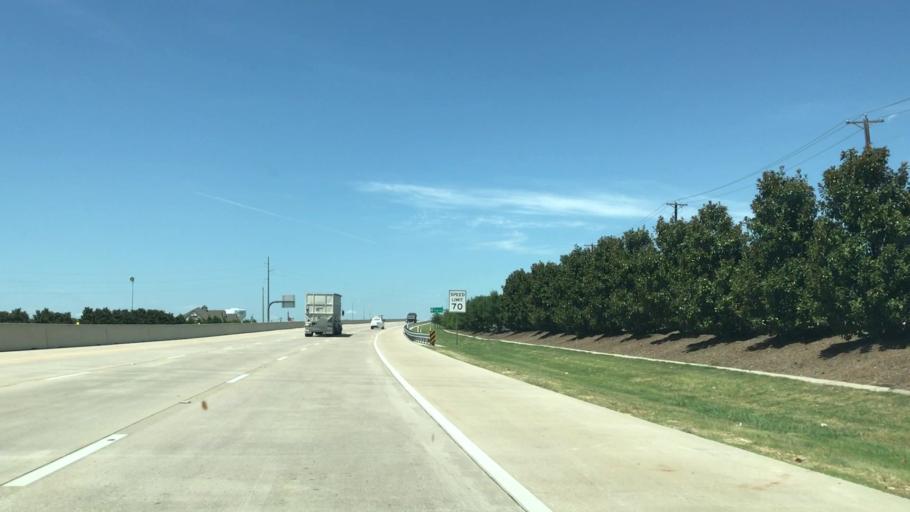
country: US
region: Texas
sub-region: Dallas County
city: Rowlett
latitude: 32.8867
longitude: -96.5565
